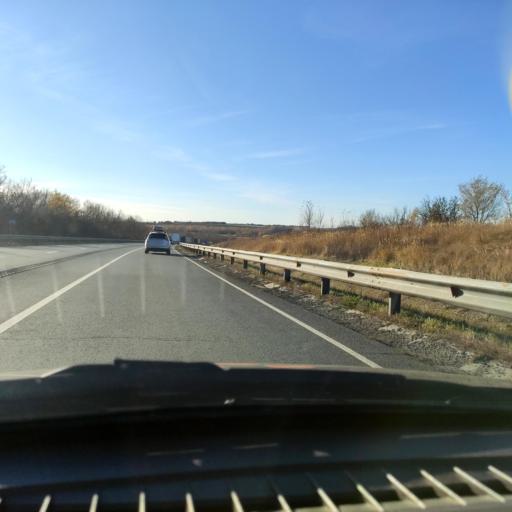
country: RU
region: Samara
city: Obsharovka
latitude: 53.2084
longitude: 48.8170
